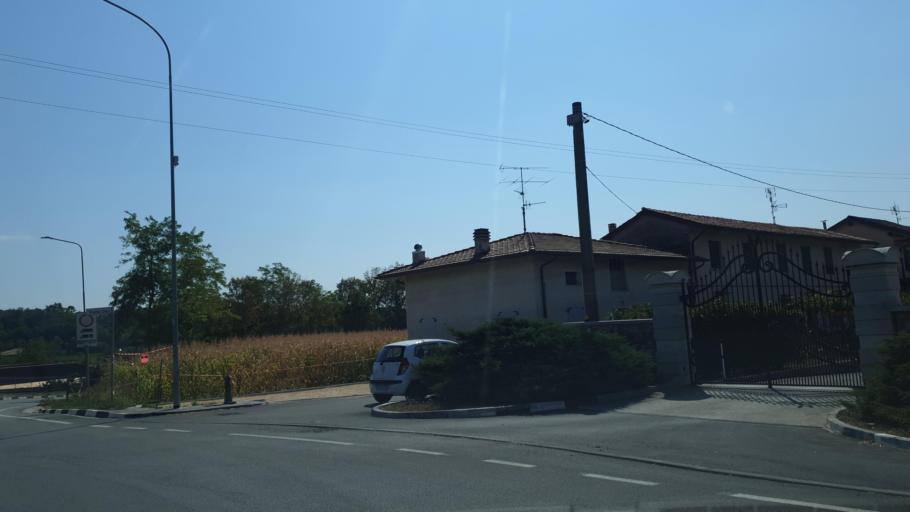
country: IT
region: Lombardy
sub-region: Provincia di Brescia
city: Prevalle
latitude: 45.5463
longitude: 10.4344
